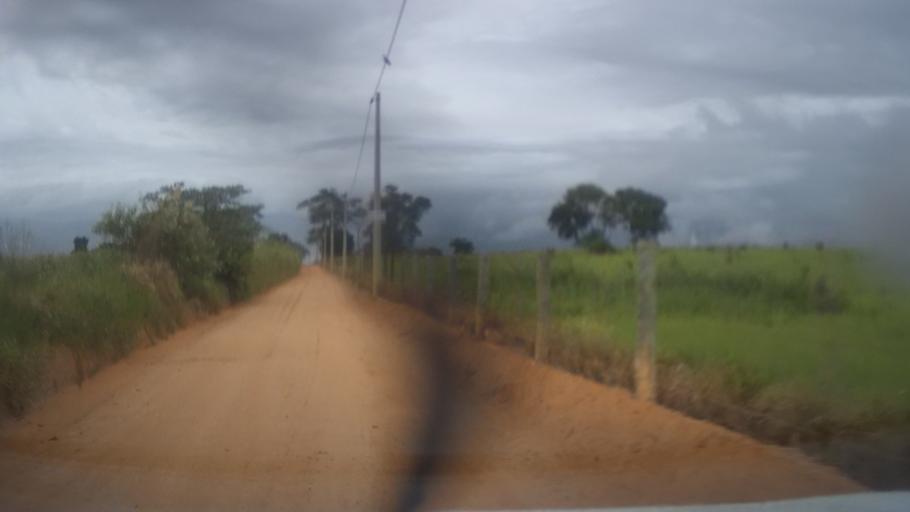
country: BR
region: Sao Paulo
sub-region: Itupeva
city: Itupeva
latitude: -23.1824
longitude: -47.0339
